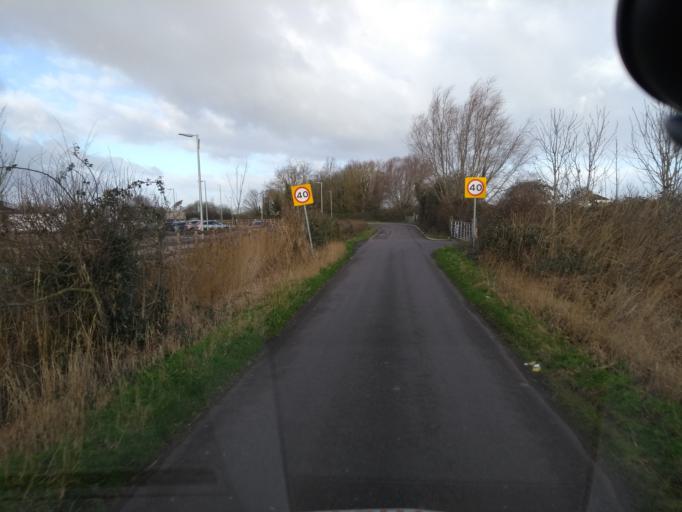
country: GB
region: England
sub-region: Somerset
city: Highbridge
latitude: 51.2279
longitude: -2.9600
